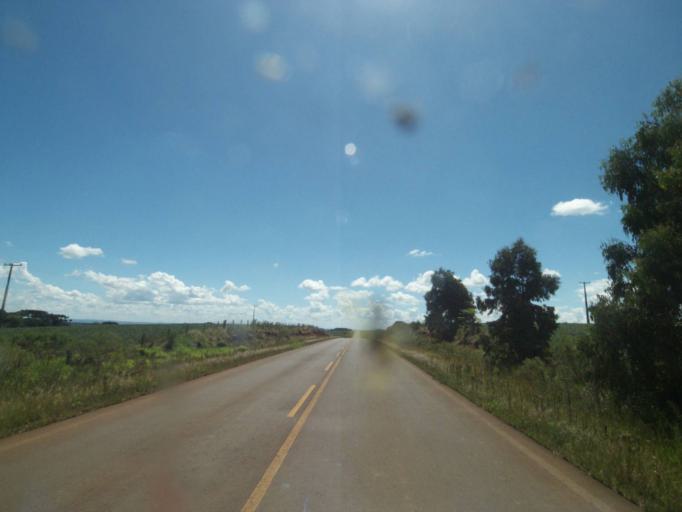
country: BR
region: Parana
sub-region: Pinhao
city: Pinhao
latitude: -25.8132
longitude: -52.0532
